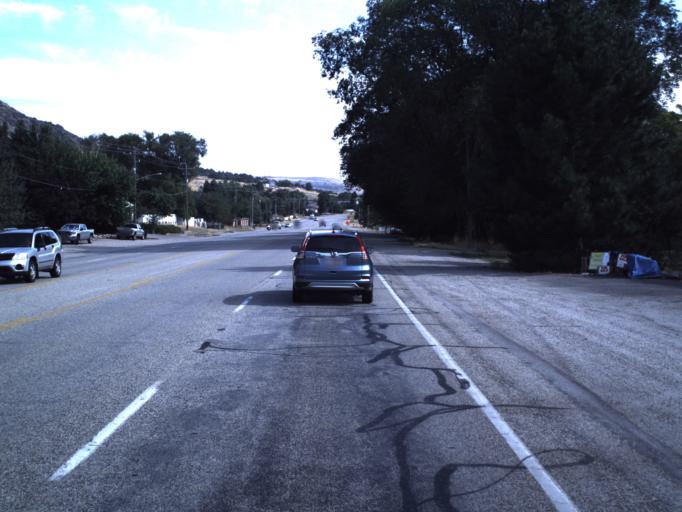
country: US
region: Utah
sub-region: Box Elder County
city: Willard
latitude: 41.4018
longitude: -112.0356
